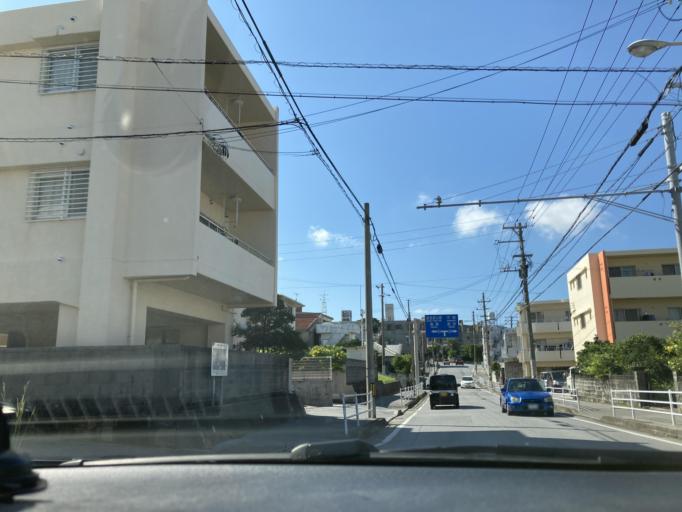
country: JP
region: Okinawa
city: Ginowan
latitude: 26.2218
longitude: 127.7342
